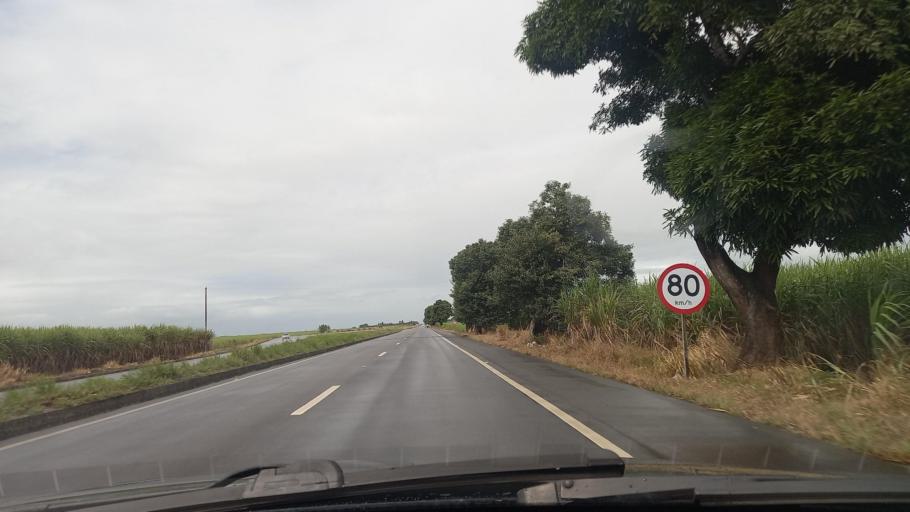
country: BR
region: Alagoas
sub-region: Campo Alegre
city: Campo Alegre
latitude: -9.8049
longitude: -36.2641
